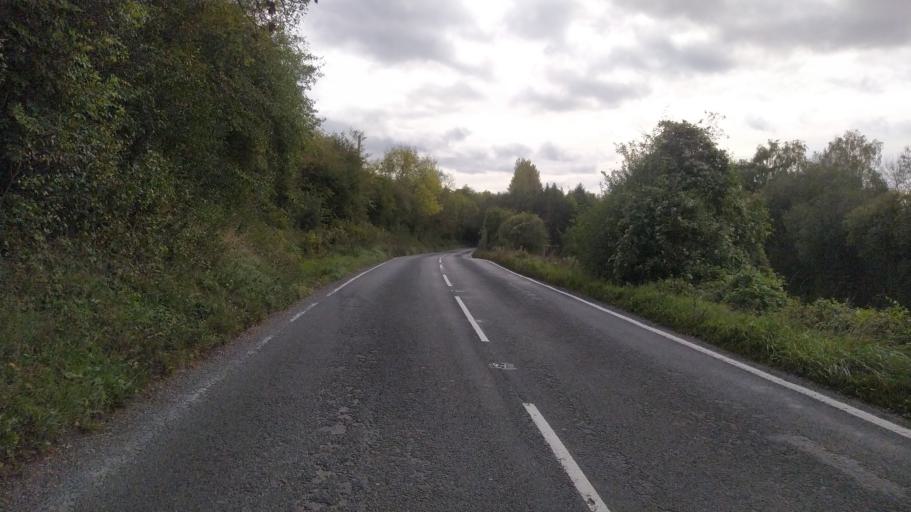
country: GB
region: England
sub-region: Hampshire
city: Romsey
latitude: 51.0534
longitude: -1.5162
